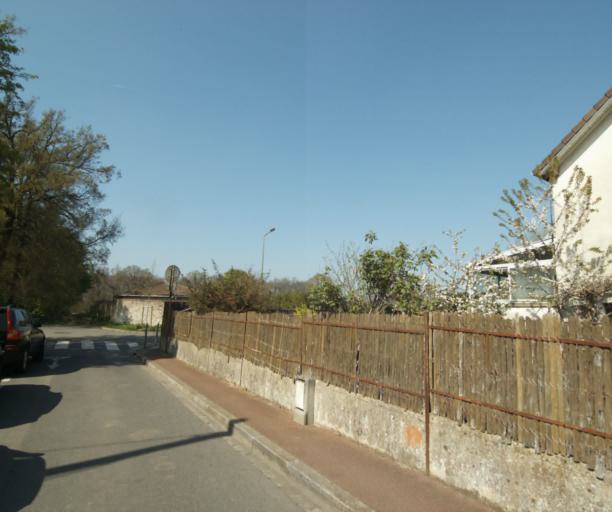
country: FR
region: Ile-de-France
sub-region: Departement des Hauts-de-Seine
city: Sevres
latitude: 48.8127
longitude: 2.2081
